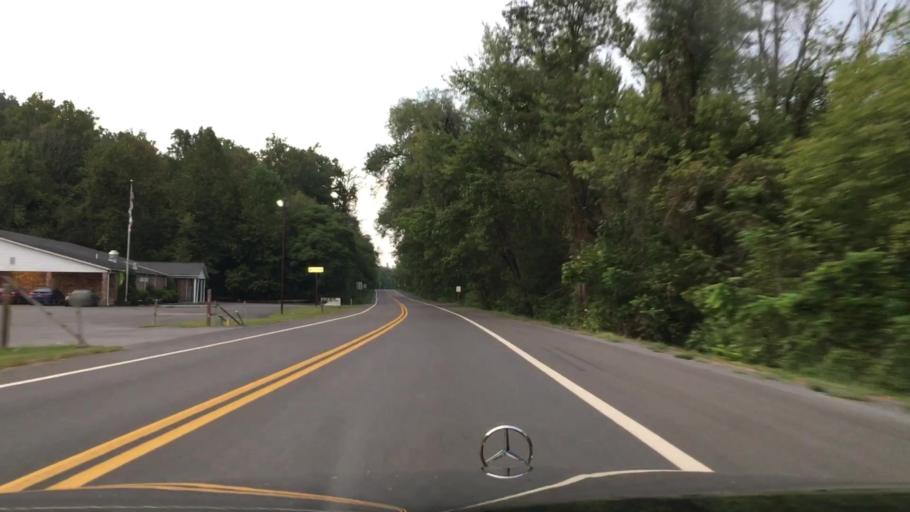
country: US
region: West Virginia
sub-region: Morgan County
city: Berkeley Springs
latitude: 39.6342
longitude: -78.2226
